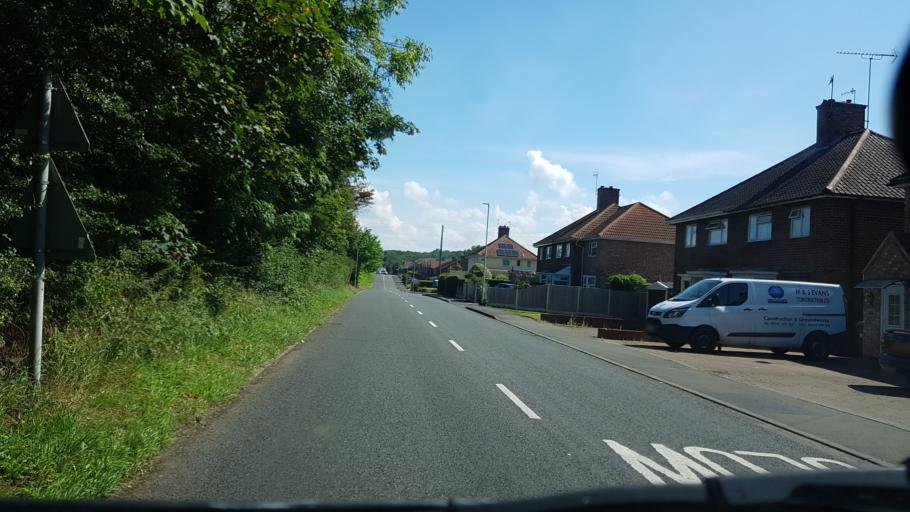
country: GB
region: England
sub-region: Worcestershire
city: Stourport-on-Severn
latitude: 52.3513
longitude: -2.2973
